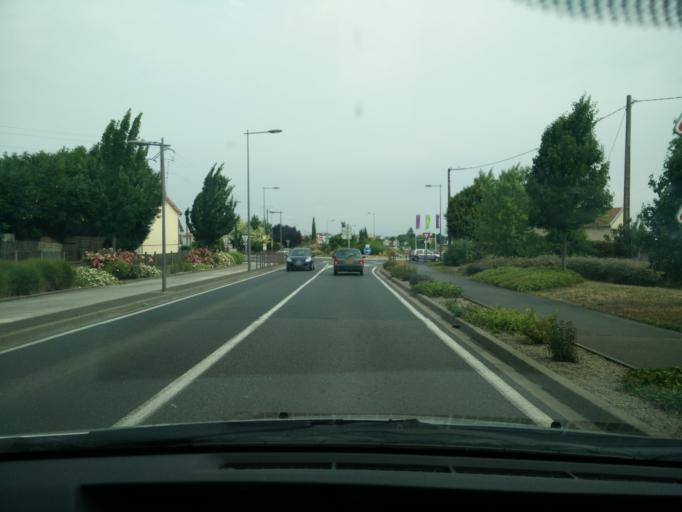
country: FR
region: Poitou-Charentes
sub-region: Departement des Deux-Sevres
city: Thouars
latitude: 46.9786
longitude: -0.1985
